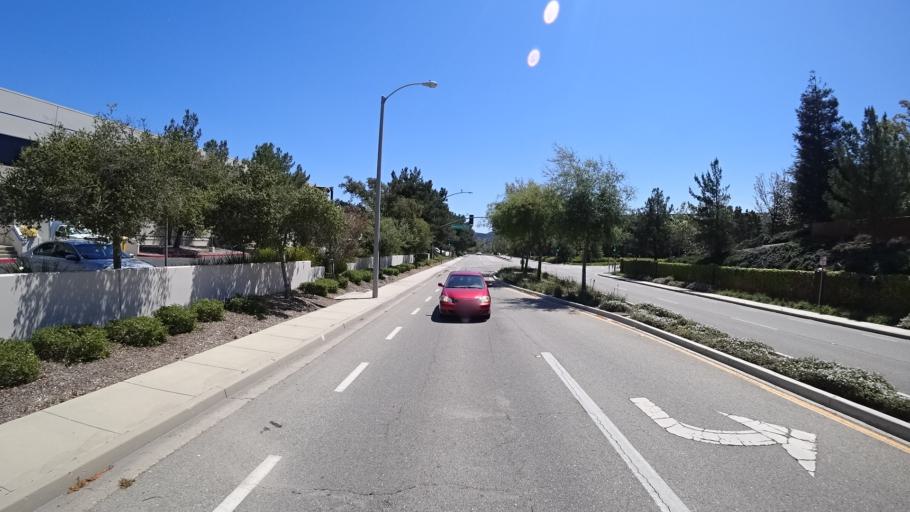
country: US
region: California
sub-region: Ventura County
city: Casa Conejo
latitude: 34.1928
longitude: -118.9189
